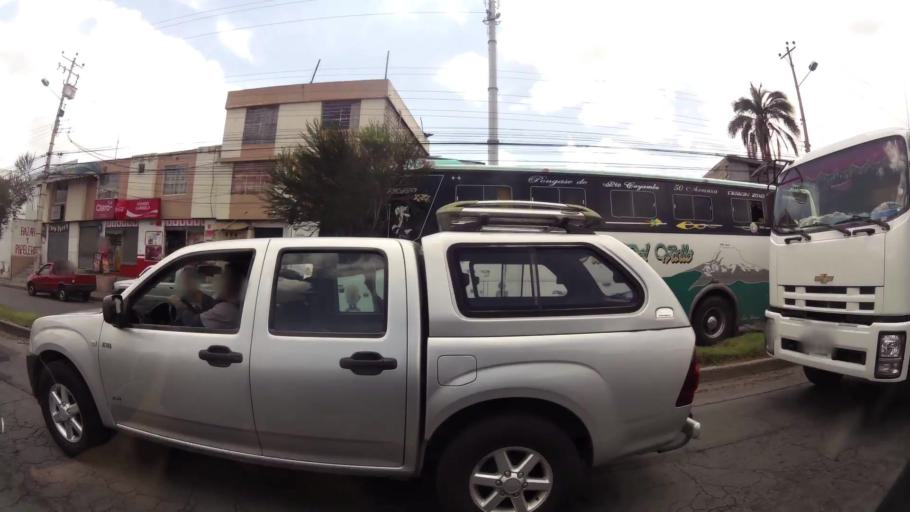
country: EC
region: Pichincha
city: Quito
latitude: -0.1068
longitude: -78.4425
